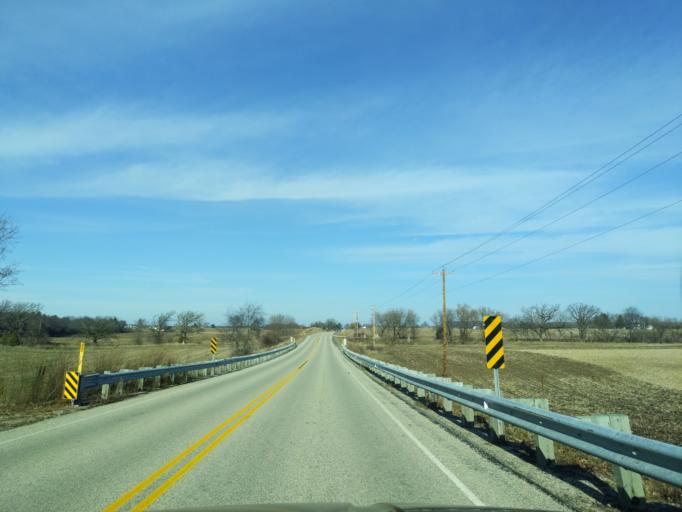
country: US
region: Wisconsin
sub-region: Jefferson County
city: Palmyra
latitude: 42.7684
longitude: -88.6031
